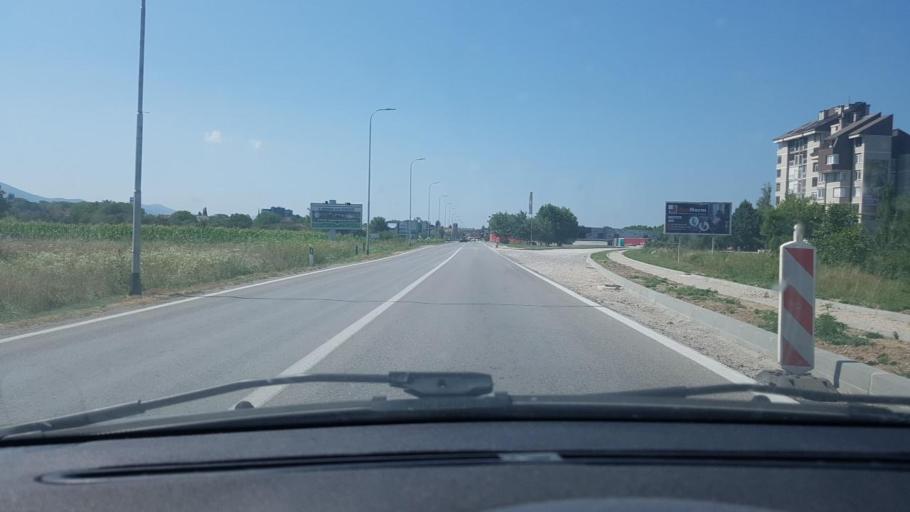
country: BA
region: Federation of Bosnia and Herzegovina
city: Bihac
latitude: 44.8102
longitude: 15.8828
